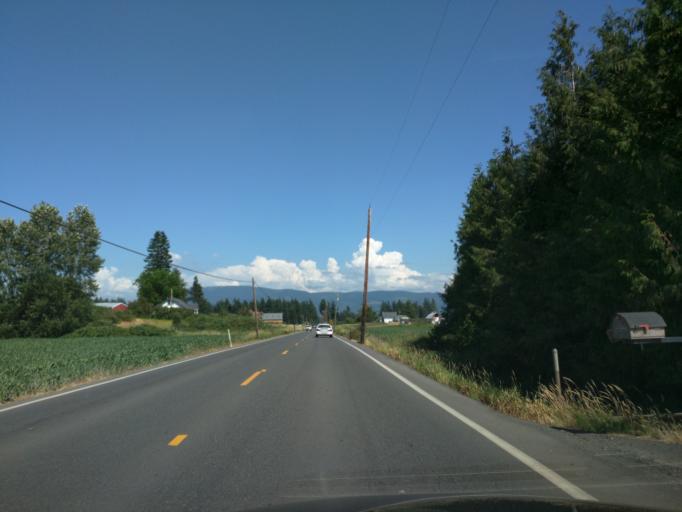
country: US
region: Washington
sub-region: Whatcom County
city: Everson
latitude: 48.8916
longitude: -122.4032
